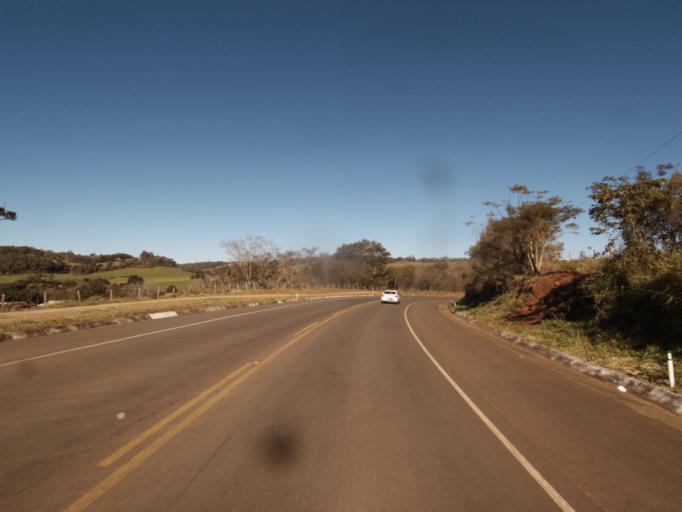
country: AR
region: Misiones
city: Bernardo de Irigoyen
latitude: -26.6847
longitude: -53.5495
